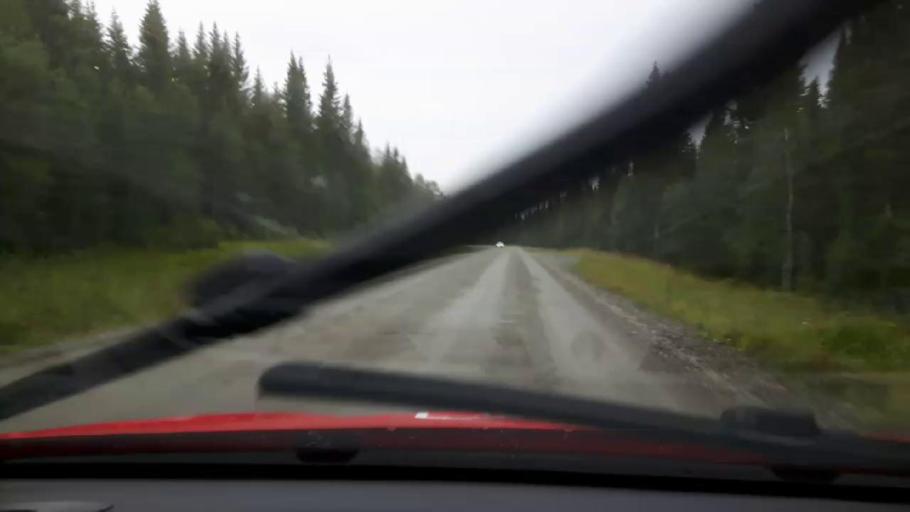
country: SE
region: Jaemtland
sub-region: Are Kommun
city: Are
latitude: 63.4519
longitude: 12.6521
